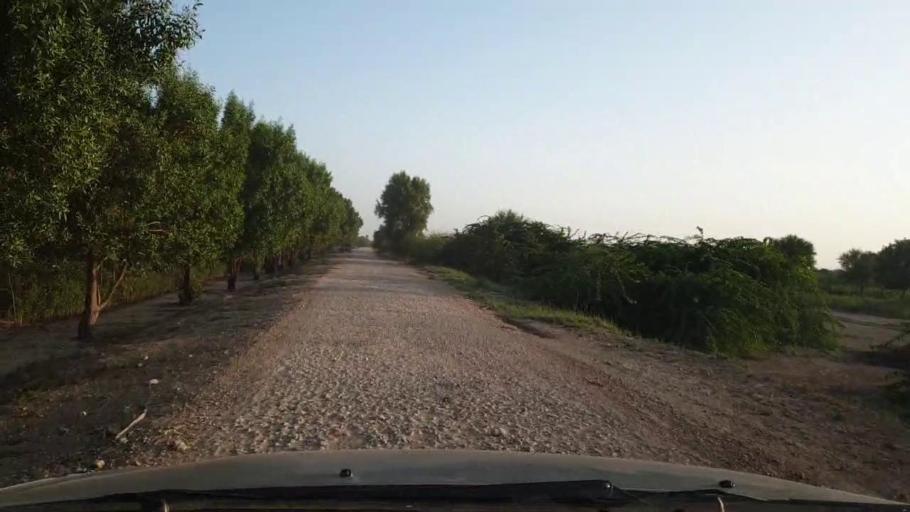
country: PK
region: Sindh
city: Tando Ghulam Ali
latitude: 25.1073
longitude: 68.9387
